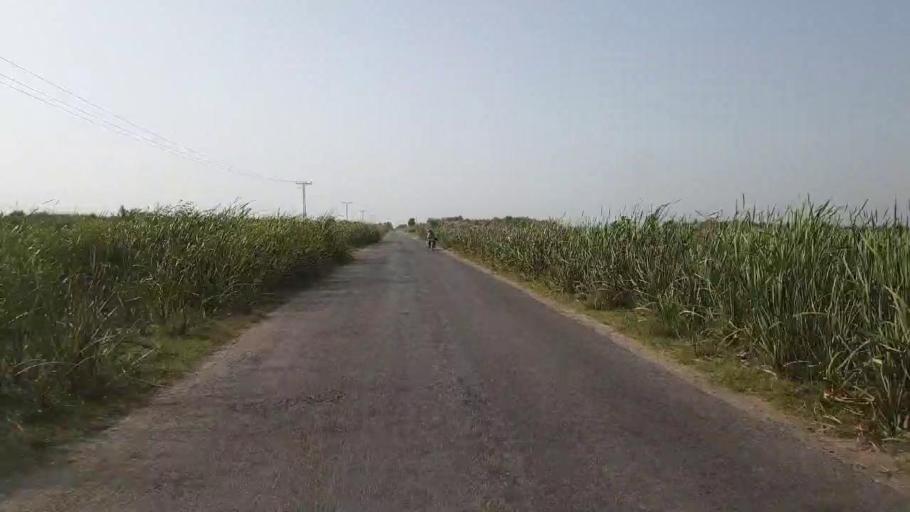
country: PK
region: Sindh
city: Khadro
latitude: 26.3531
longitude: 68.9220
